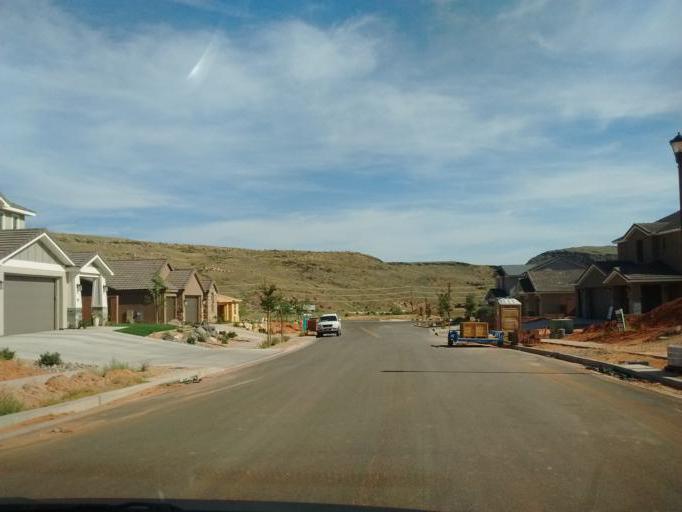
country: US
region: Utah
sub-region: Washington County
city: Washington
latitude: 37.1357
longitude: -113.4813
